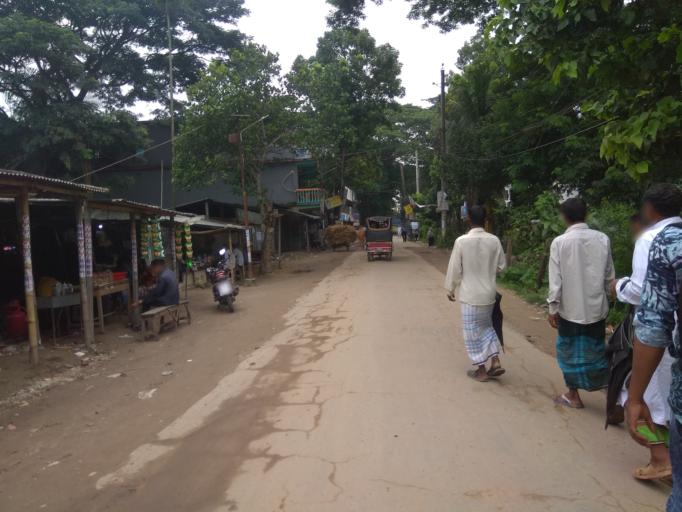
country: BD
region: Dhaka
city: Dohar
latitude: 23.4733
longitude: 90.0259
